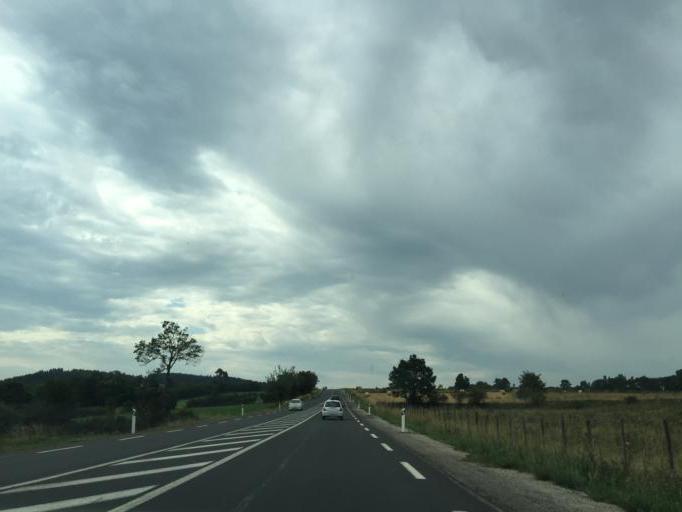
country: FR
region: Auvergne
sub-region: Departement de la Haute-Loire
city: Solignac-sur-Loire
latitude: 44.9106
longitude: 3.8491
